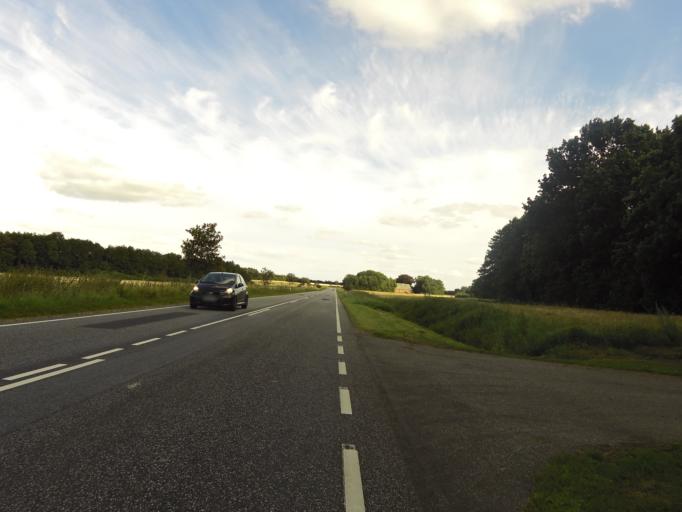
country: DK
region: South Denmark
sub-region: Tonder Kommune
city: Toftlund
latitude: 55.2153
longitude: 9.0330
